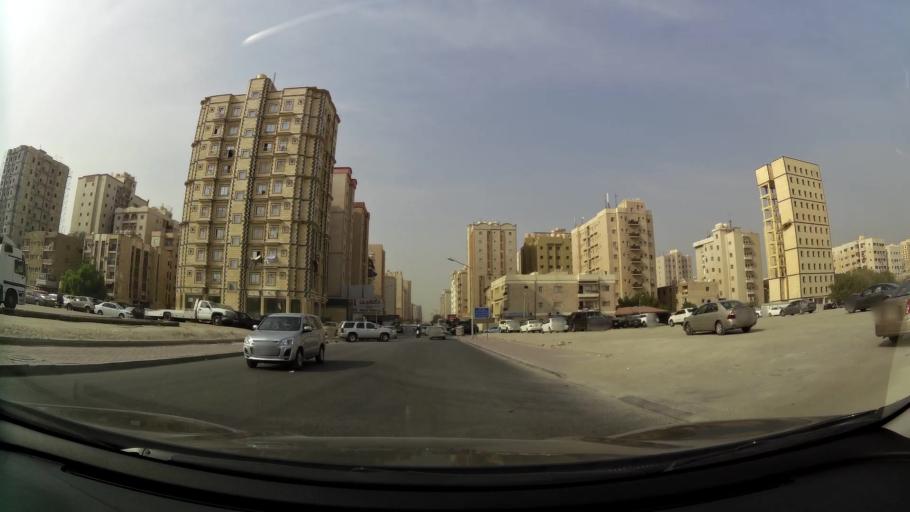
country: KW
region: Al Farwaniyah
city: Al Farwaniyah
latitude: 29.2727
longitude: 47.9571
